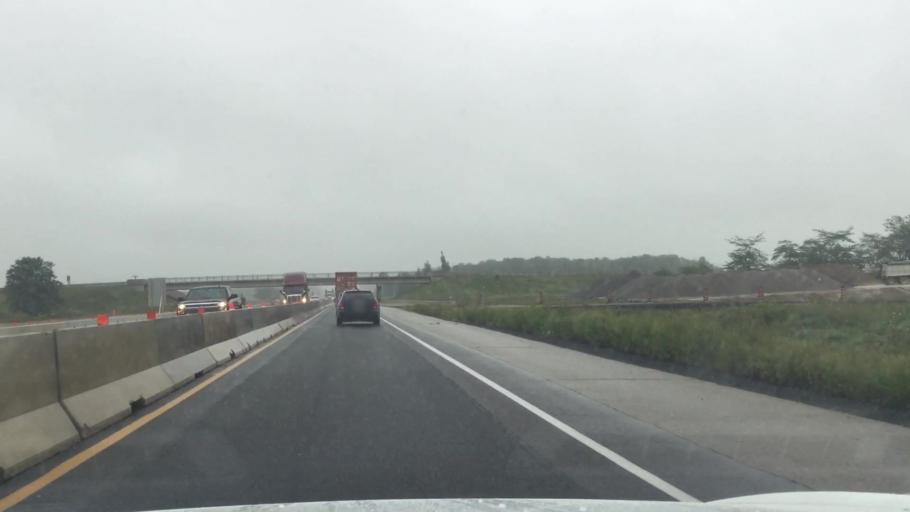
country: CA
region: Ontario
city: Delaware
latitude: 42.7707
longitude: -81.3816
